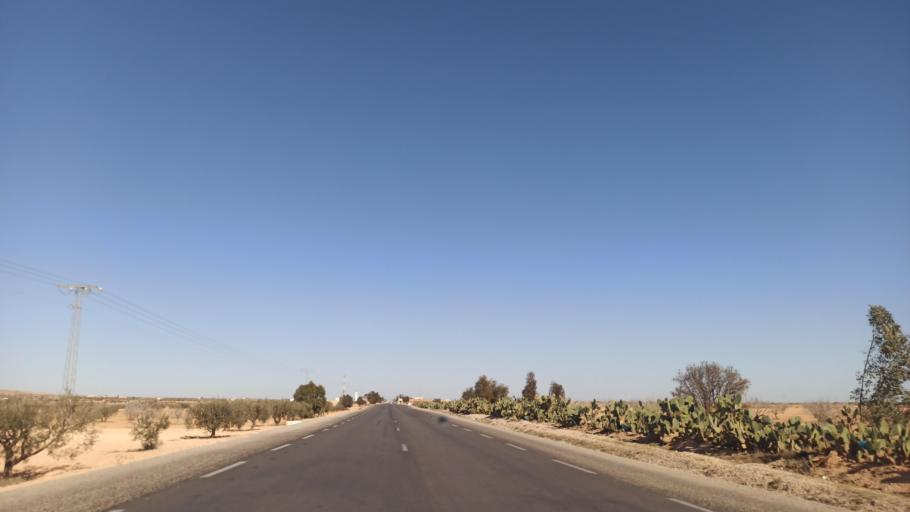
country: TN
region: Sidi Bu Zayd
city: Bi'r al Hufayy
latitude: 34.7339
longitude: 9.0691
